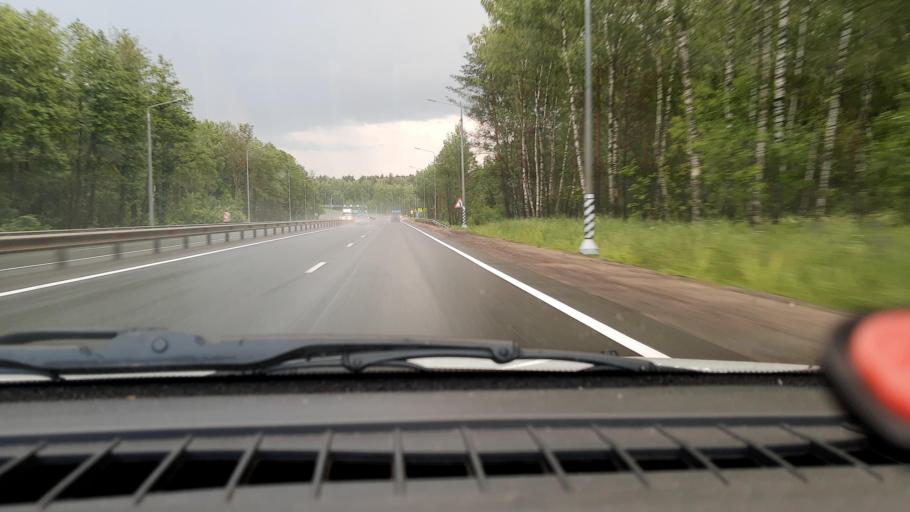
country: RU
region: Nizjnij Novgorod
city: Burevestnik
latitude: 56.0826
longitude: 43.9209
